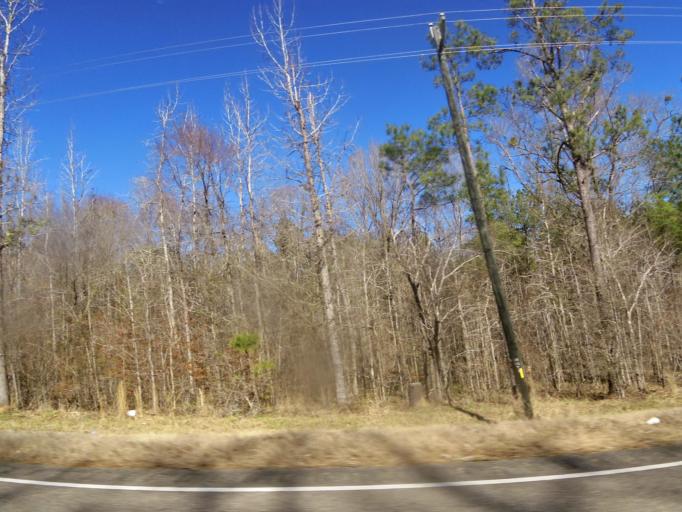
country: US
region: Alabama
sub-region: Montgomery County
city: Pike Road
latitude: 32.1896
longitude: -86.1099
